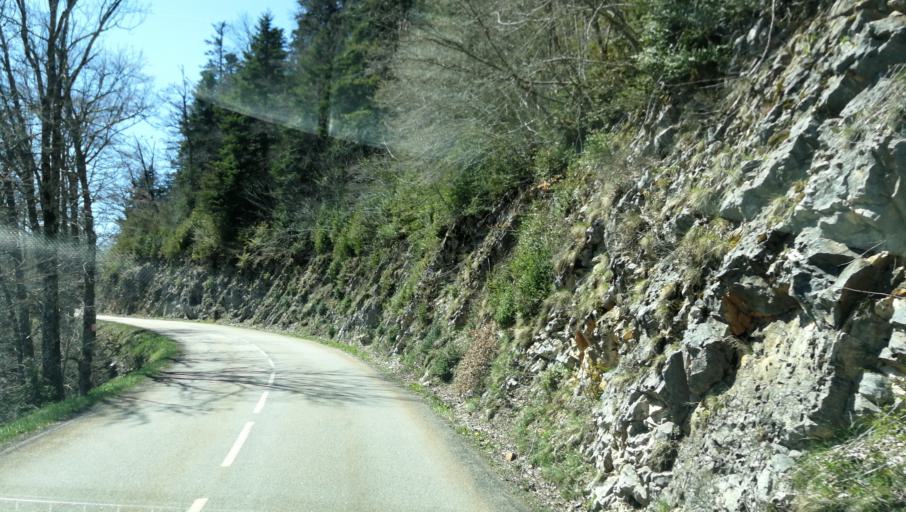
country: FR
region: Rhone-Alpes
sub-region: Departement de la Drome
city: Die
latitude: 44.8682
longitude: 5.4067
